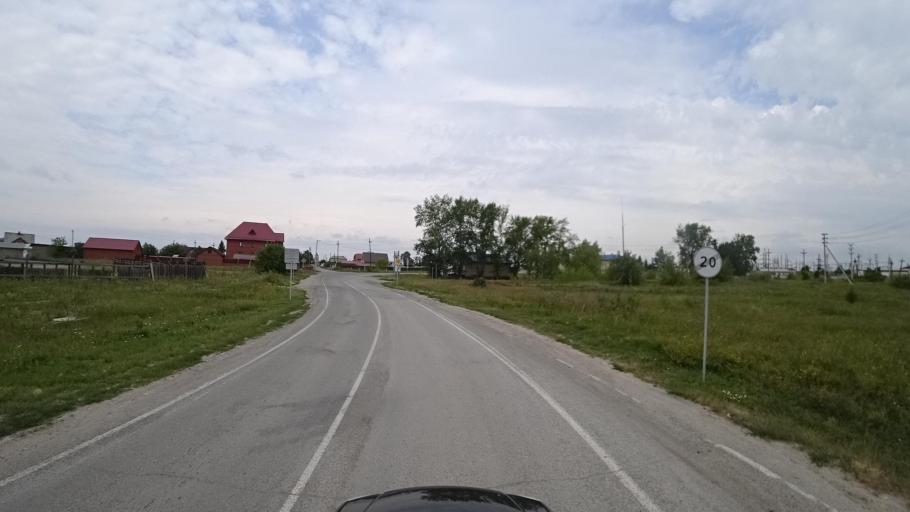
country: RU
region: Sverdlovsk
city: Kamyshlov
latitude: 56.8476
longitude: 62.7447
